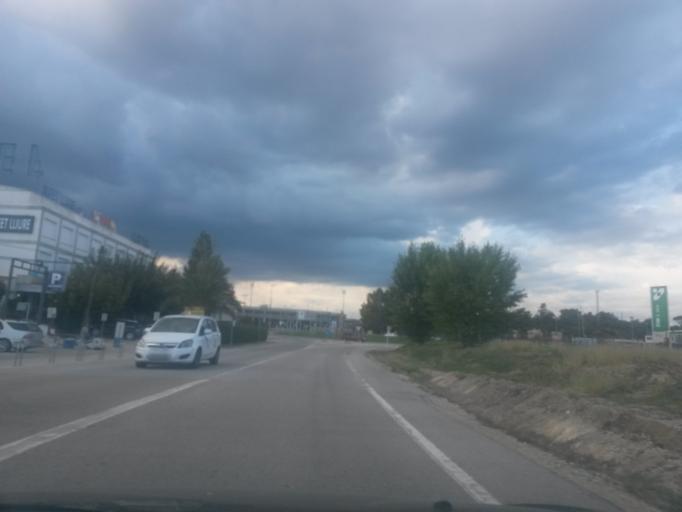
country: ES
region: Catalonia
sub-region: Provincia de Girona
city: Vilobi d'Onyar
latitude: 41.8987
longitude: 2.7696
